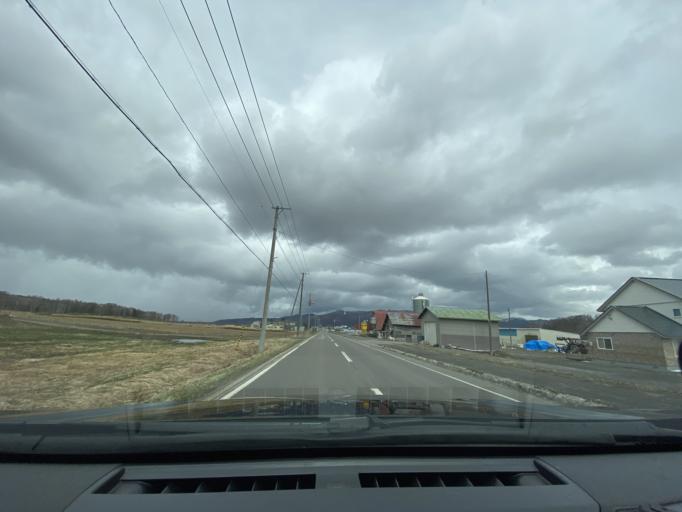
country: JP
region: Hokkaido
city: Nayoro
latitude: 44.1037
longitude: 142.4767
